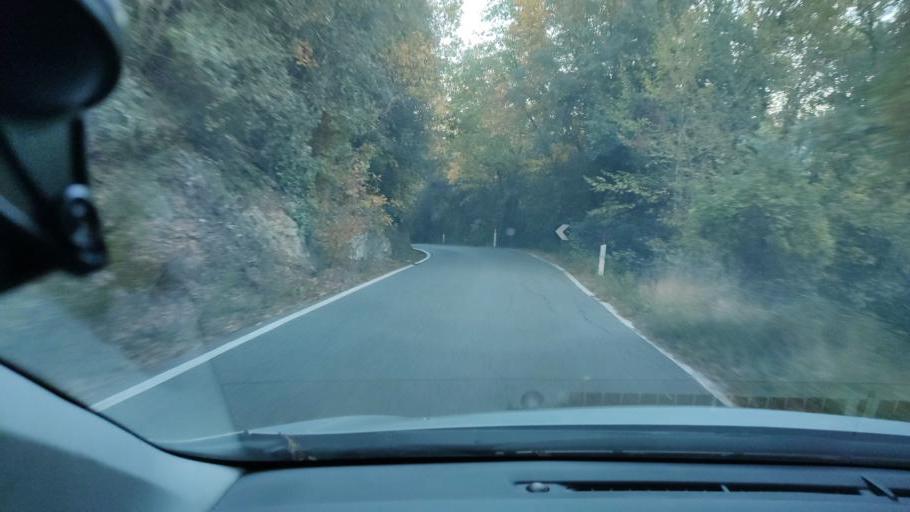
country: IT
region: Umbria
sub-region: Provincia di Terni
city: Amelia
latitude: 42.5880
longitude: 12.4311
